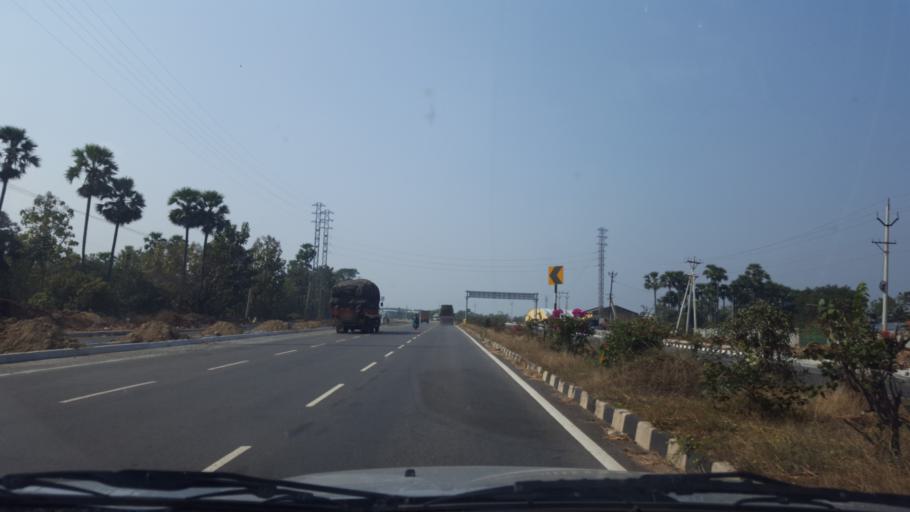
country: IN
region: Andhra Pradesh
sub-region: Vizianagaram District
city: Vizianagaram
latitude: 18.0228
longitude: 83.4880
